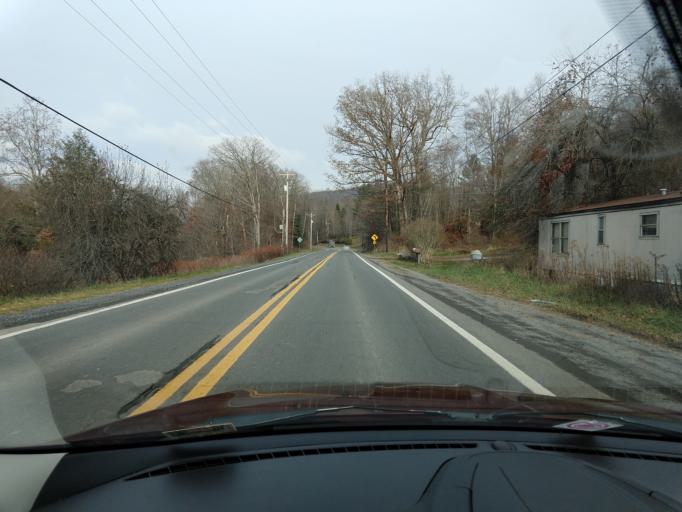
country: US
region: West Virginia
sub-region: Greenbrier County
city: Rainelle
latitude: 37.9770
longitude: -80.7107
